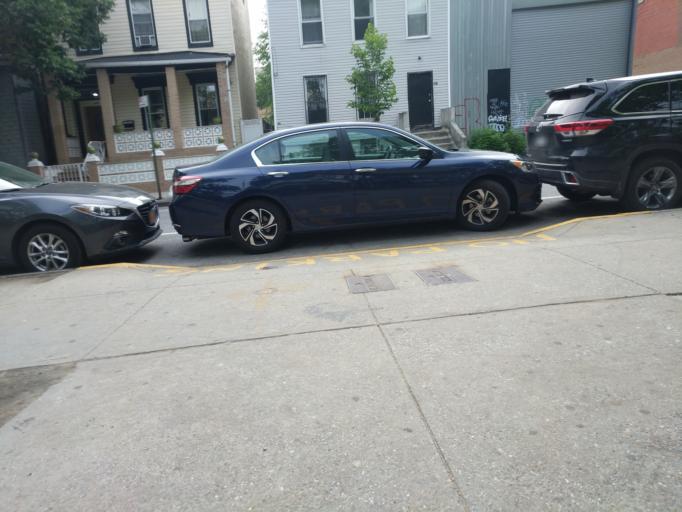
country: US
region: New York
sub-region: Kings County
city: Brooklyn
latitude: 40.6917
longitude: -73.9577
